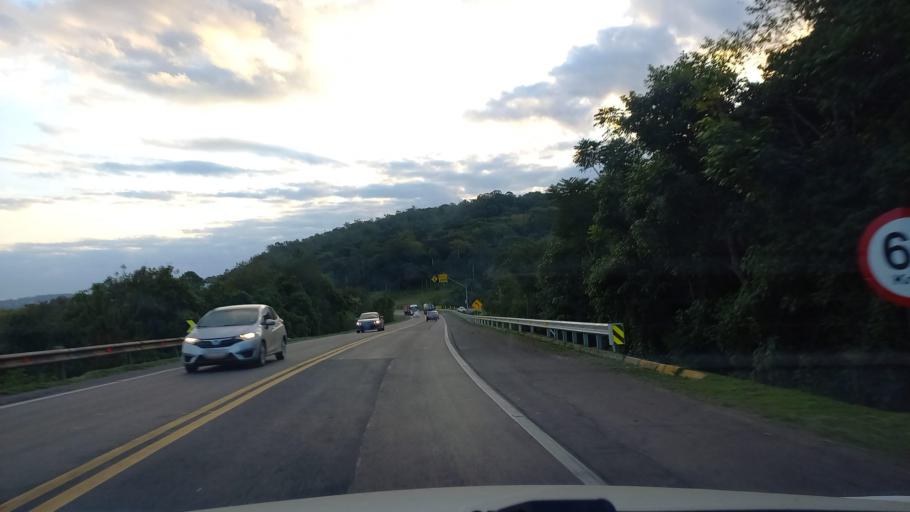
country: BR
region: Rio Grande do Sul
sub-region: Santa Cruz Do Sul
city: Santa Cruz do Sul
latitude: -29.6849
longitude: -52.4396
